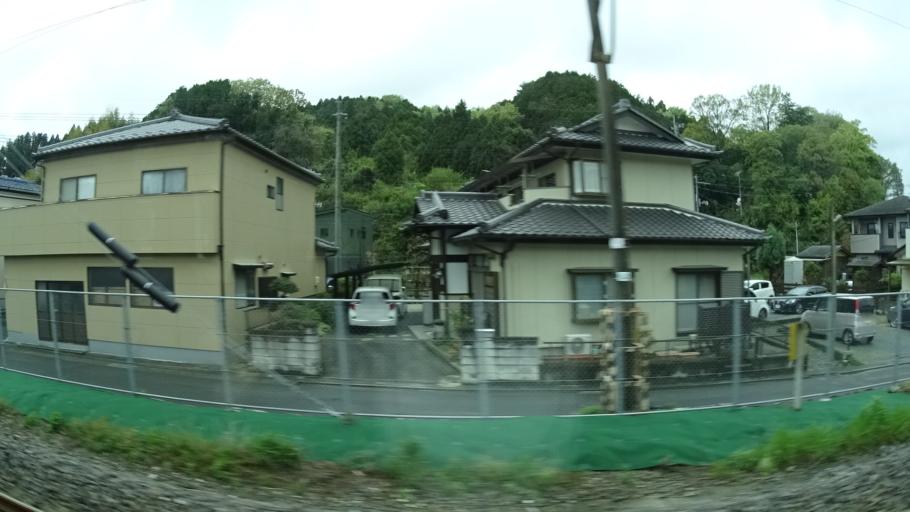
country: JP
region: Fukushima
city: Iwaki
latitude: 37.0161
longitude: 140.8460
